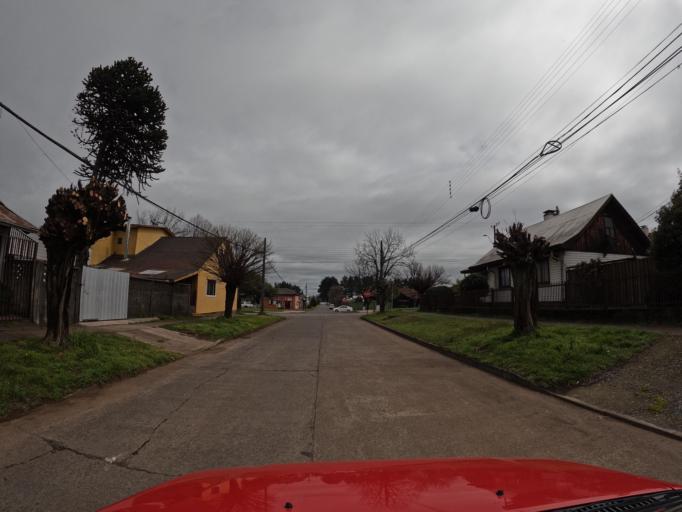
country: CL
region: Araucania
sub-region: Provincia de Malleco
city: Victoria
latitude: -38.2314
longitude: -72.3358
